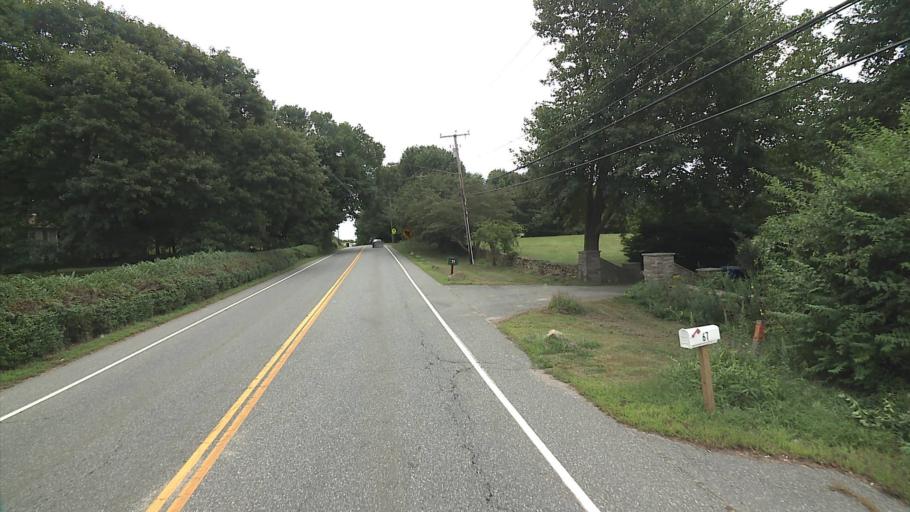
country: US
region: Connecticut
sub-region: Middlesex County
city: Old Saybrook Center
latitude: 41.2993
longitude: -72.3248
